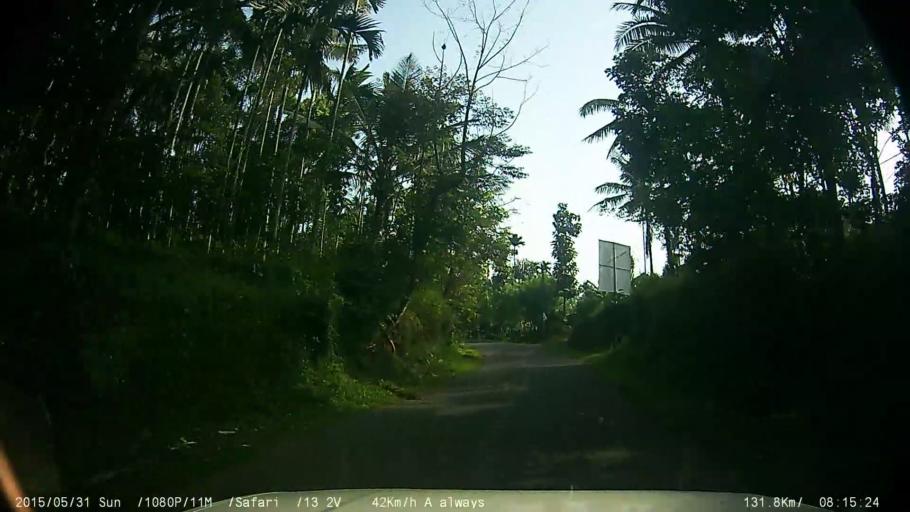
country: IN
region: Kerala
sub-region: Wayanad
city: Kalpetta
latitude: 11.6495
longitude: 76.0024
